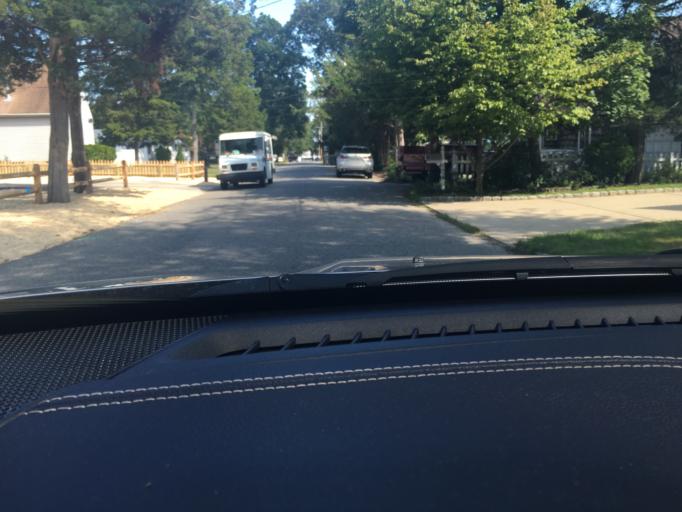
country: US
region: New Jersey
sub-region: Ocean County
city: Leisure Village East
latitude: 40.0537
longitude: -74.1289
